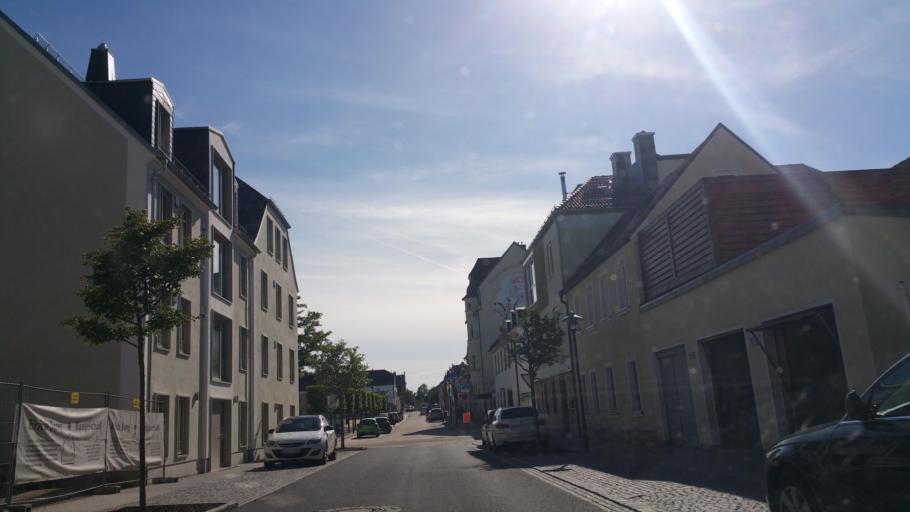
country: DE
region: Bavaria
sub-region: Upper Franconia
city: Rehau
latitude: 50.2487
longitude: 12.0362
